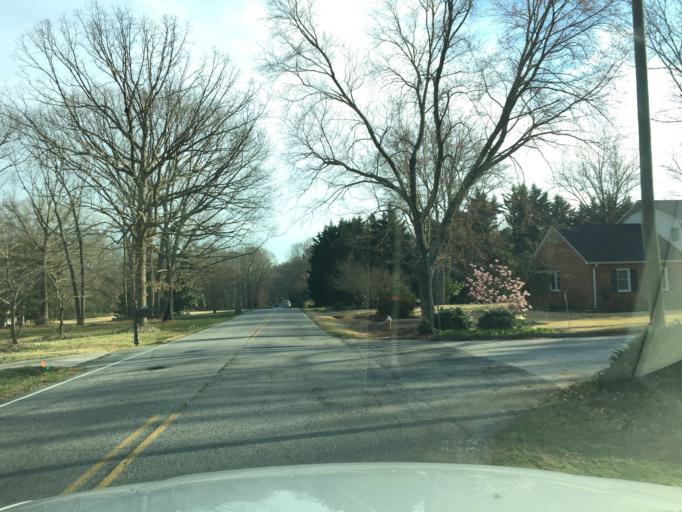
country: US
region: South Carolina
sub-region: Greenville County
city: Wade Hampton
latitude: 34.8630
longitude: -82.2945
